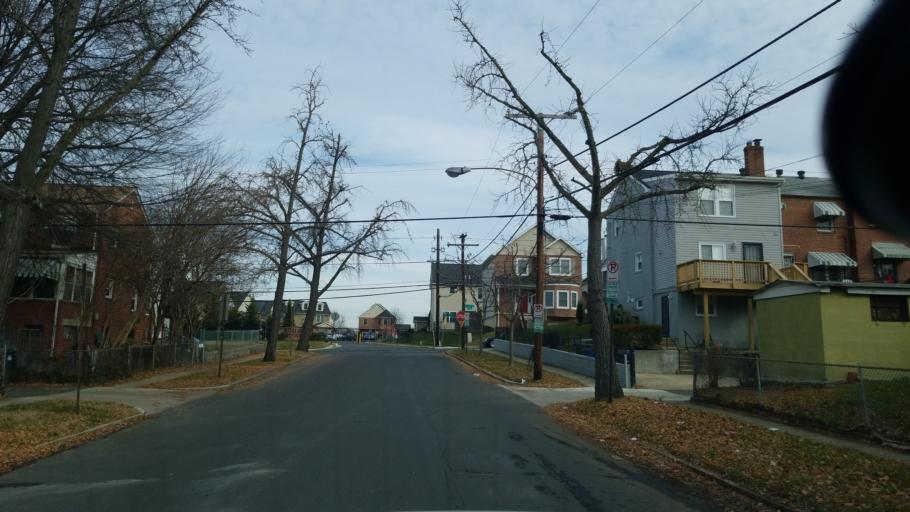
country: US
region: Maryland
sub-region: Prince George's County
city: Hillcrest Heights
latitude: 38.8656
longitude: -76.9760
